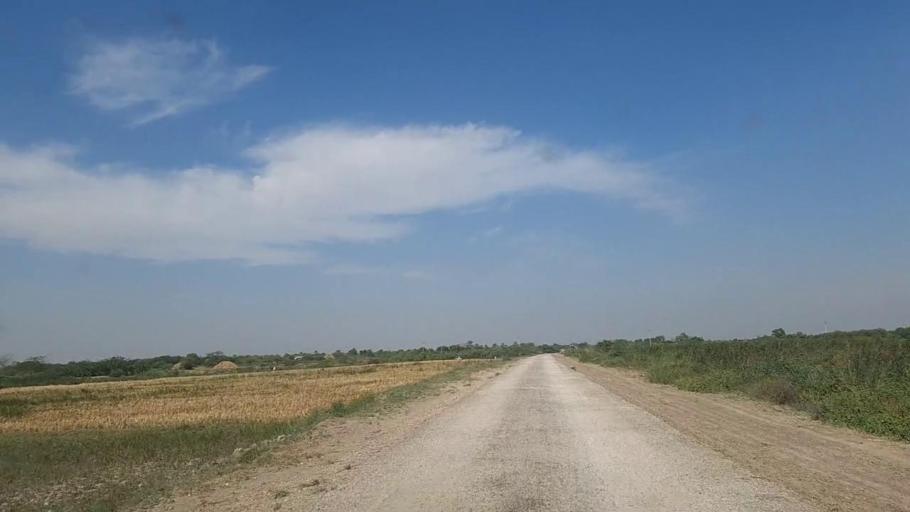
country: PK
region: Sindh
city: Bulri
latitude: 24.8382
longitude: 68.2740
